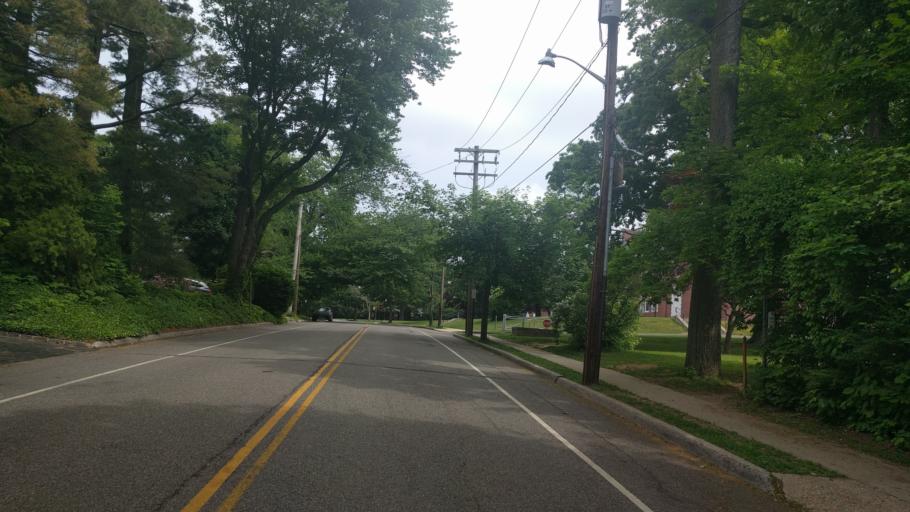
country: US
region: New York
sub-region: Nassau County
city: Glenwood Landing
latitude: 40.8274
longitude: -73.6367
